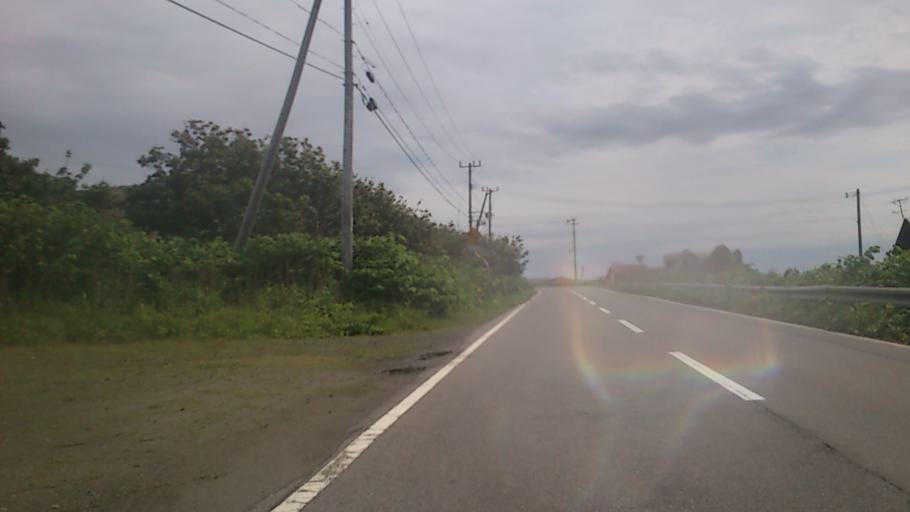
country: JP
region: Akita
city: Noshiromachi
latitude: 40.4593
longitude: 139.9441
